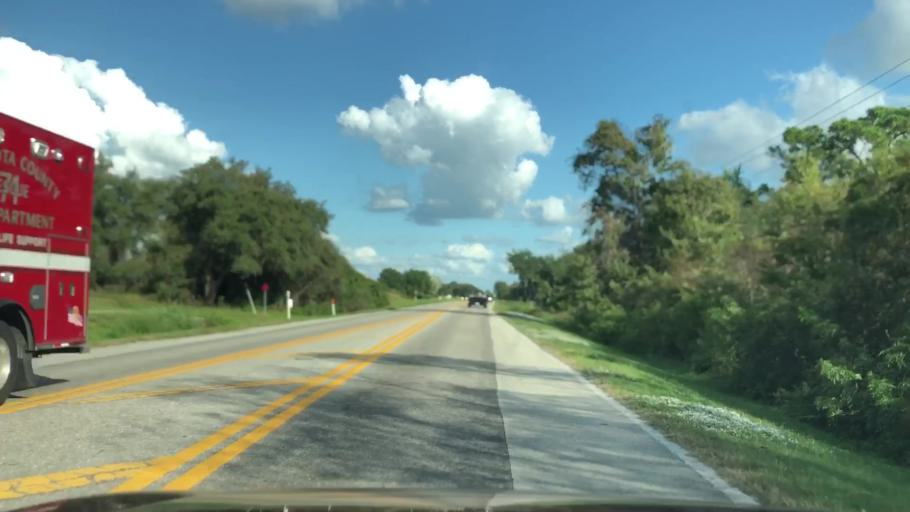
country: US
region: Florida
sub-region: Sarasota County
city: Fruitville
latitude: 27.3384
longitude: -82.4023
